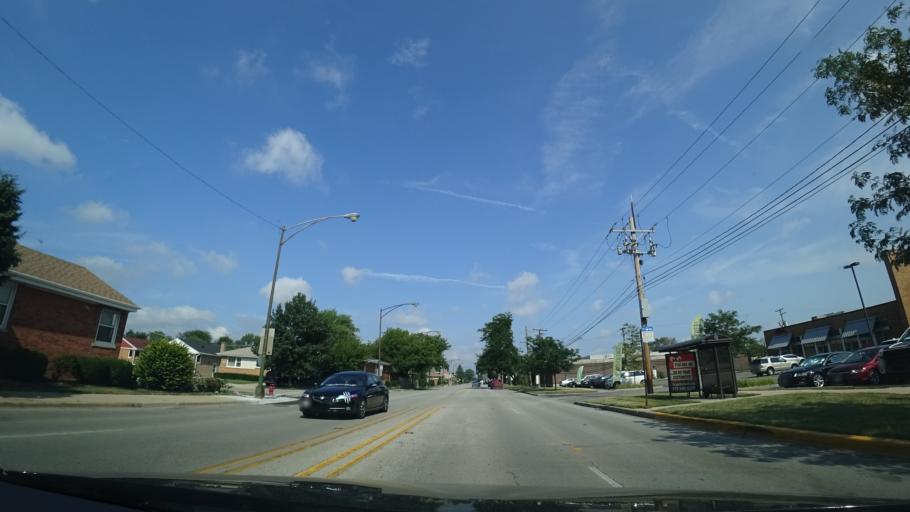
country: US
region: Illinois
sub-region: Cook County
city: Harwood Heights
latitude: 41.9683
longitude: -87.8054
